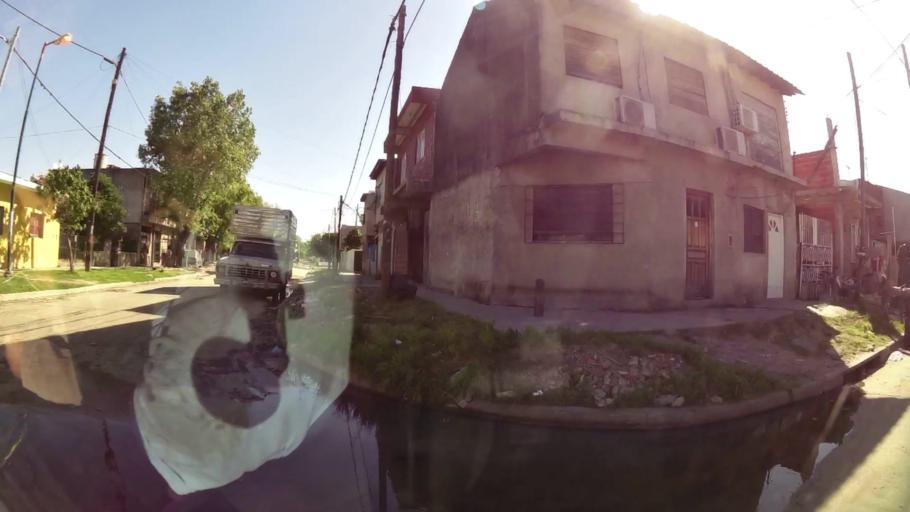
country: AR
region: Buenos Aires
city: Caseros
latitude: -34.5428
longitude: -58.5931
